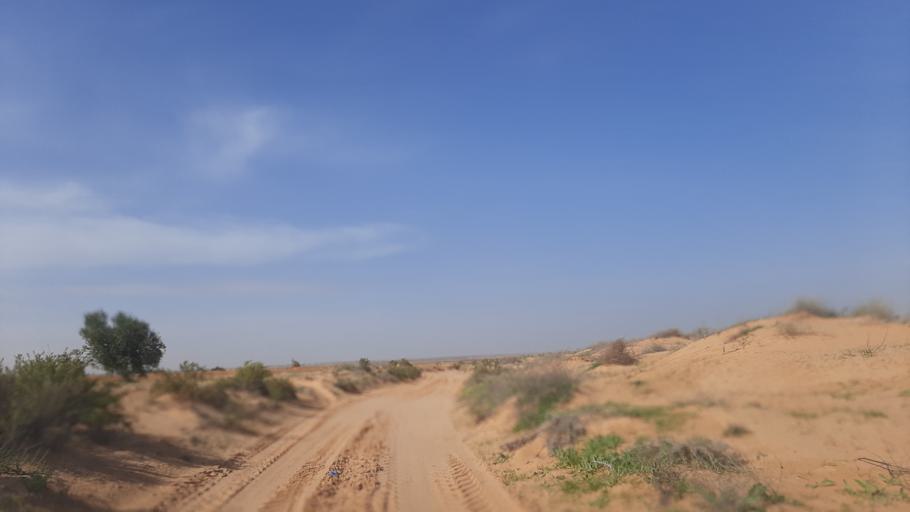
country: TN
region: Madanin
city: Zarzis
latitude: 33.4371
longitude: 10.8077
